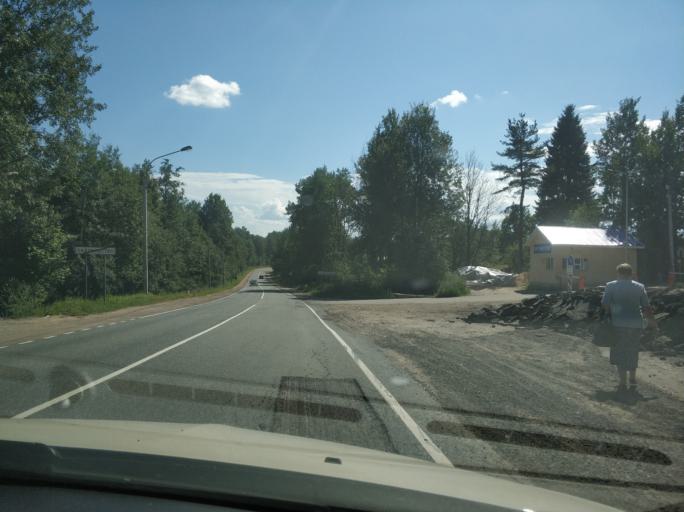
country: RU
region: Leningrad
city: Osel'ki
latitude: 60.2229
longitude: 30.5628
